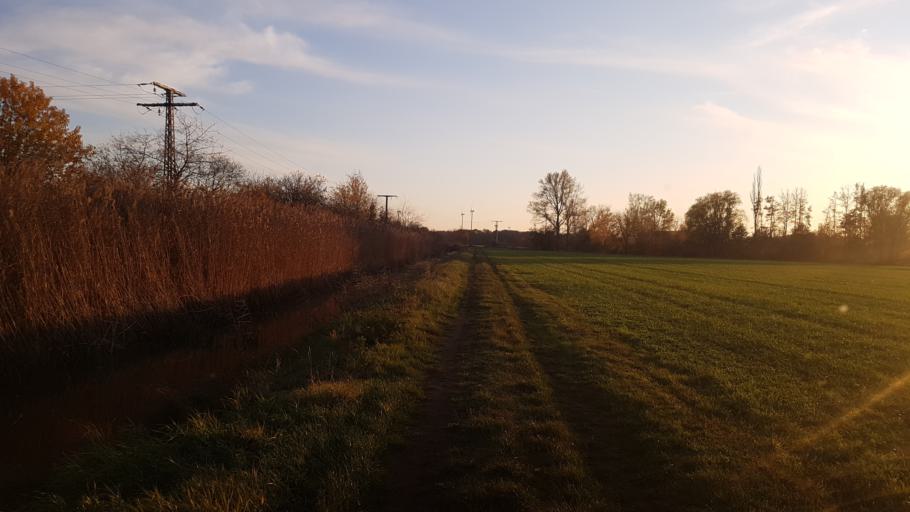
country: DE
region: Brandenburg
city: Schilda
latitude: 51.6018
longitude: 13.3155
